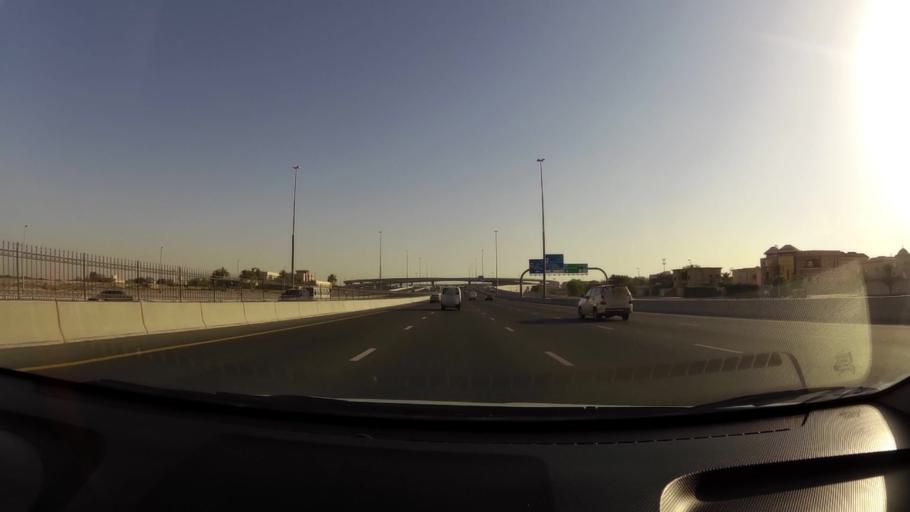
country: AE
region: Ash Shariqah
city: Sharjah
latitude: 25.3405
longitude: 55.4694
